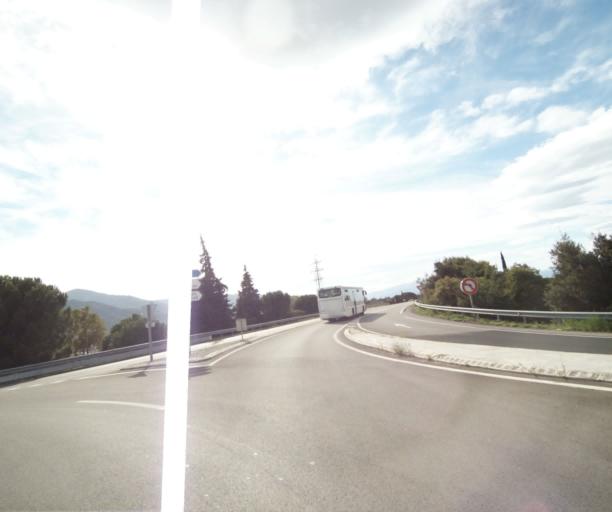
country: FR
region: Languedoc-Roussillon
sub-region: Departement des Pyrenees-Orientales
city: Argelers
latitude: 42.5511
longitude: 3.0074
